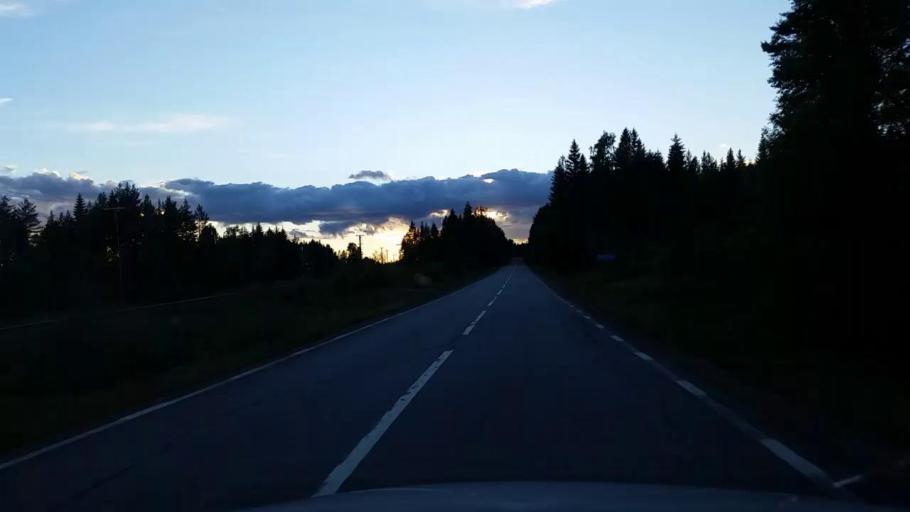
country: SE
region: Gaevleborg
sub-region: Ljusdals Kommun
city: Farila
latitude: 62.0865
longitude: 15.8110
